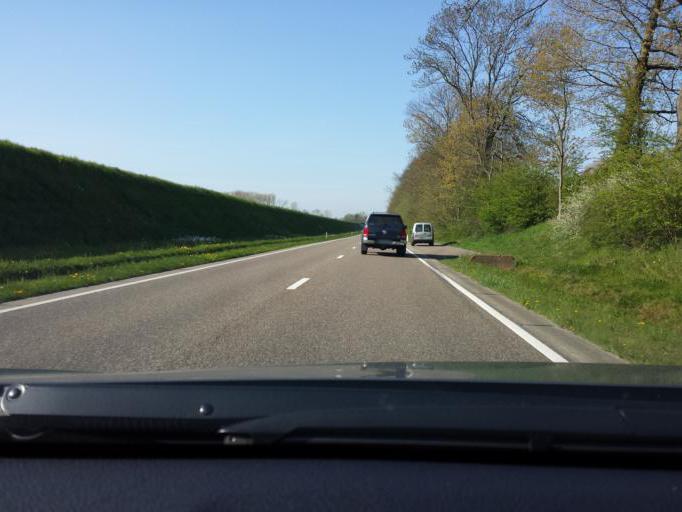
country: BE
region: Flanders
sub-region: Provincie Limburg
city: Maasmechelen
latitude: 50.9635
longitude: 5.7080
